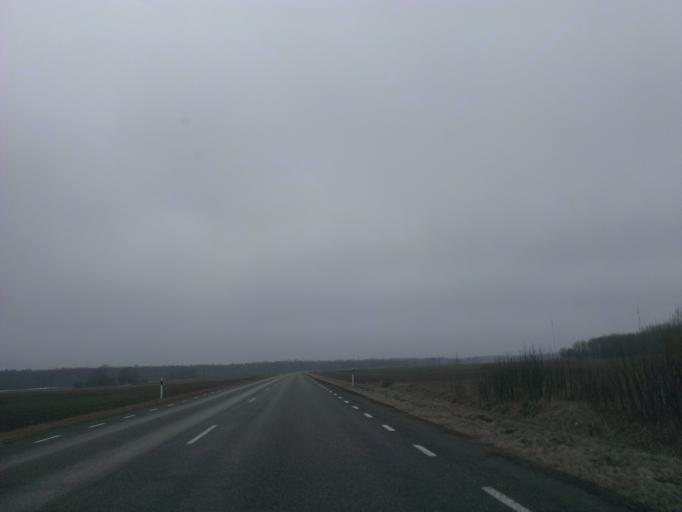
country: EE
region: Paernumaa
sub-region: Audru vald
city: Audru
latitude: 58.4931
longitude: 24.1342
